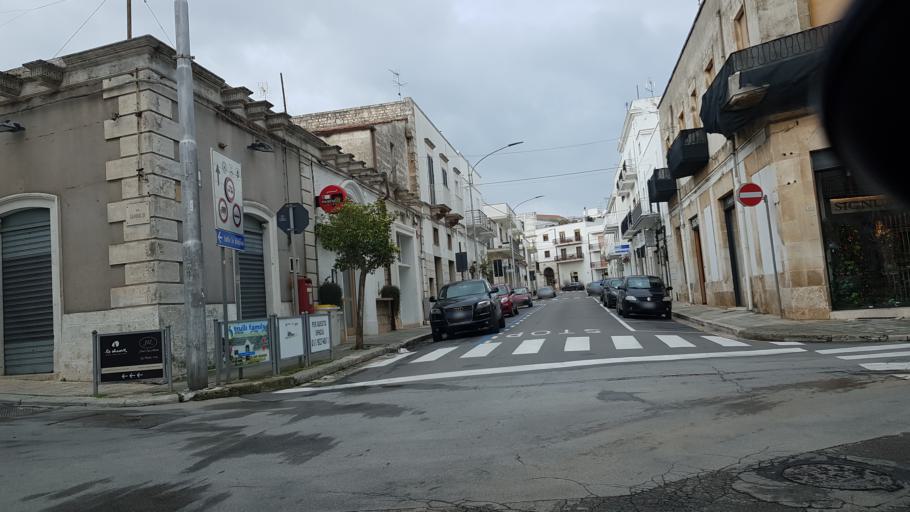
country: IT
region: Apulia
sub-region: Provincia di Bari
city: Alberobello
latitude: 40.7856
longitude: 17.2404
